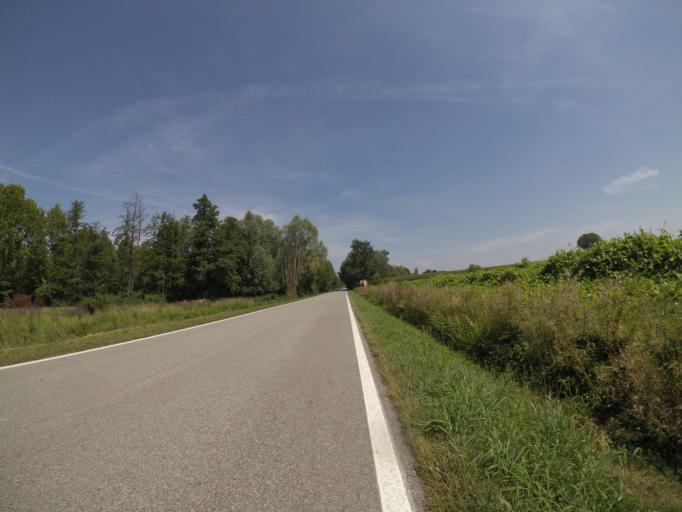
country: IT
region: Friuli Venezia Giulia
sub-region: Provincia di Udine
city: Camino al Tagliamento
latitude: 45.9070
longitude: 12.9648
